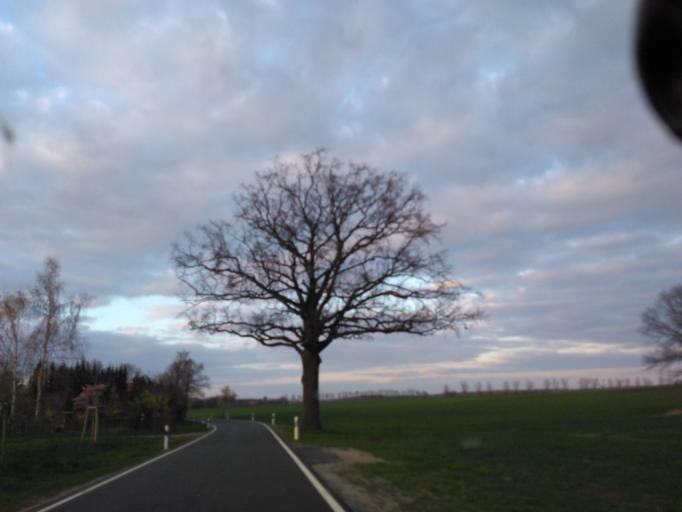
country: DE
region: Brandenburg
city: Buckow
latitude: 52.6350
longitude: 14.0724
